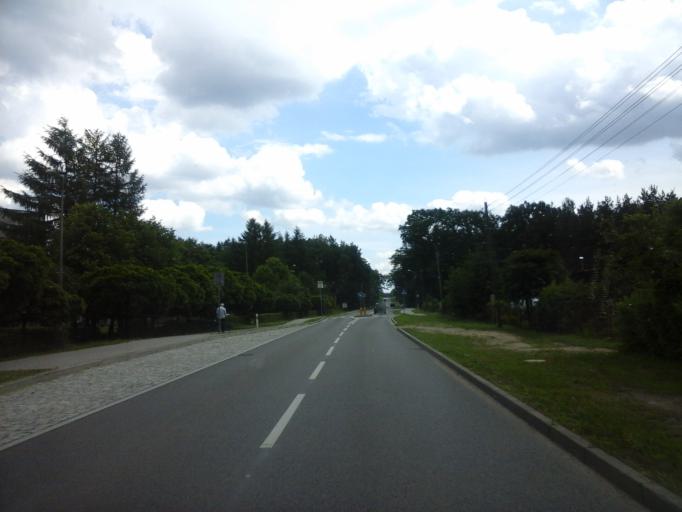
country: PL
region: West Pomeranian Voivodeship
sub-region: Powiat swidwinski
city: Slawoborze
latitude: 53.8877
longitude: 15.7161
